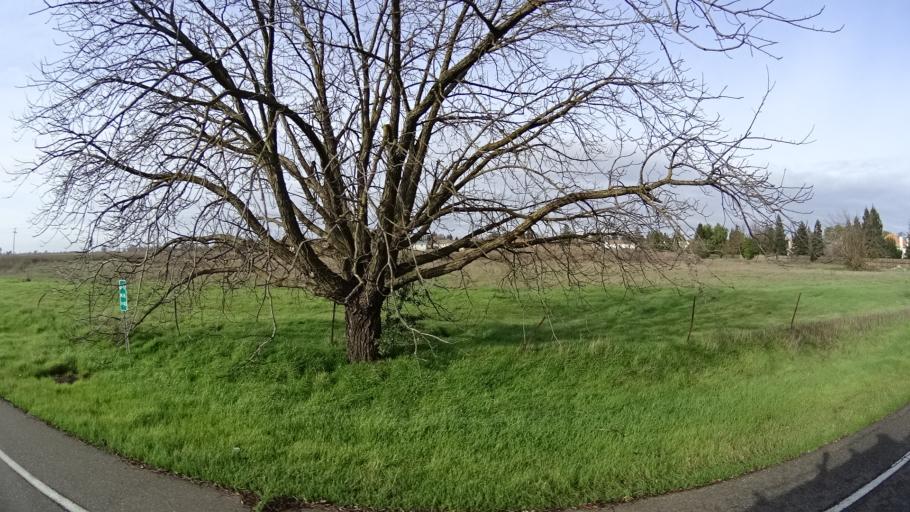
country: US
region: California
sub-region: Yolo County
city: Davis
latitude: 38.5400
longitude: -121.6946
